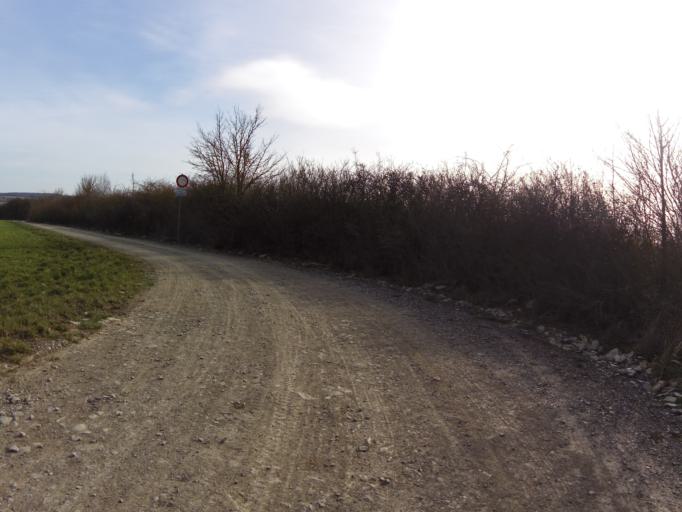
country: DE
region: Bavaria
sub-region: Regierungsbezirk Unterfranken
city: Hettstadt
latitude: 49.8263
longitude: 9.8205
